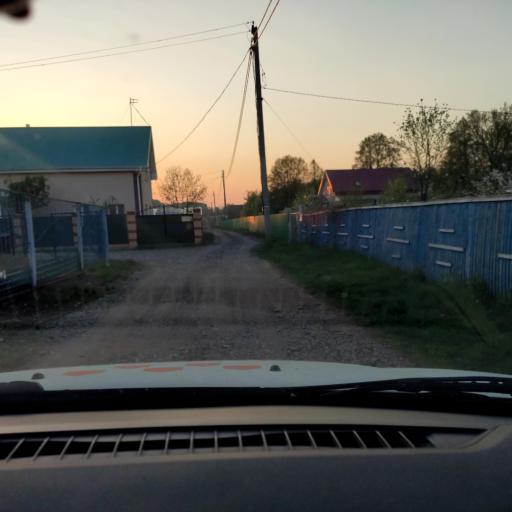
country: RU
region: Bashkortostan
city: Avdon
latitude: 54.4909
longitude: 55.8345
